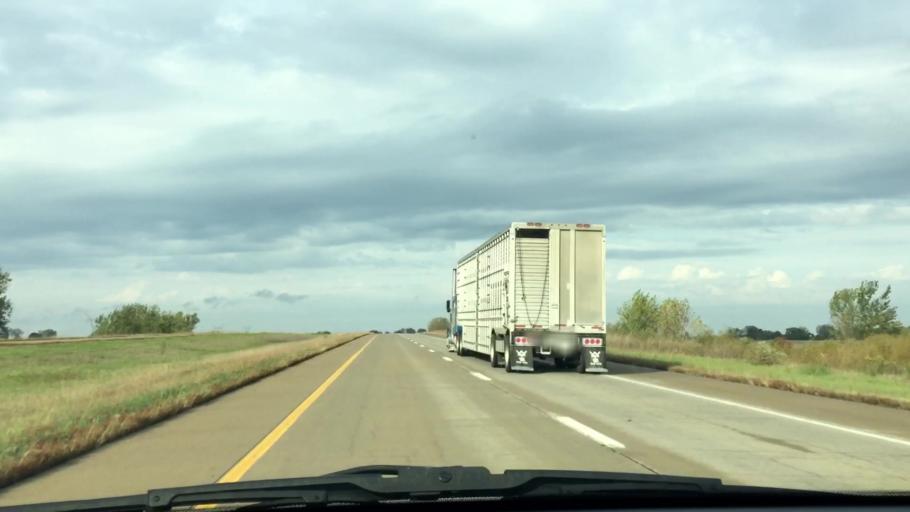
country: US
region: Illinois
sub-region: Whiteside County
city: Sterling
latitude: 41.7657
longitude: -89.8297
